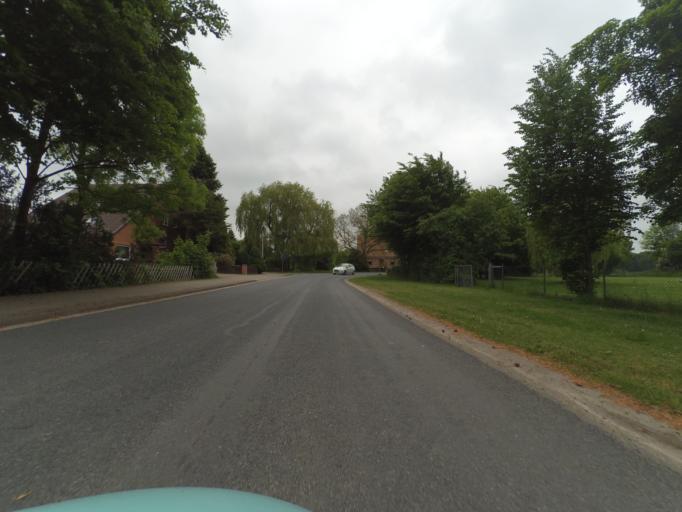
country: DE
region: Lower Saxony
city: Edemissen
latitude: 52.4264
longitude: 10.3057
